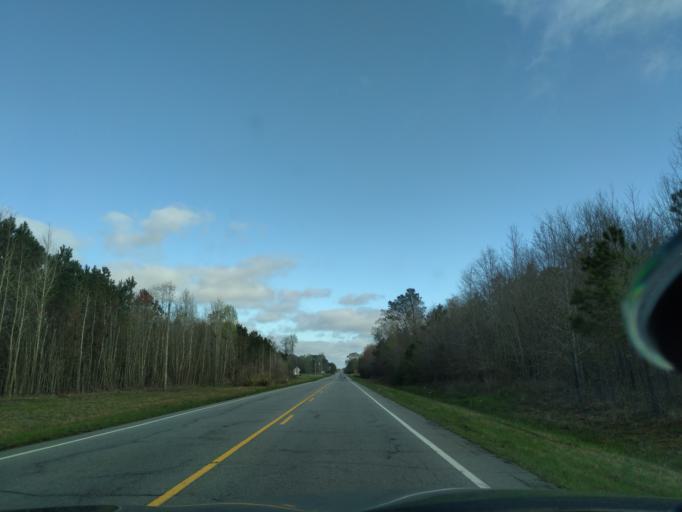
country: US
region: North Carolina
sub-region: Washington County
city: Plymouth
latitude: 36.0123
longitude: -76.7769
